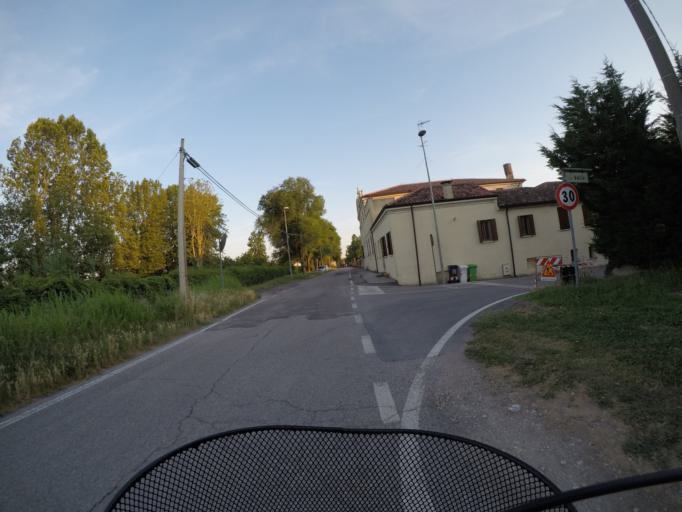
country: IT
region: Veneto
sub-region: Provincia di Rovigo
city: Fratta Polesine
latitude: 45.0350
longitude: 11.6411
